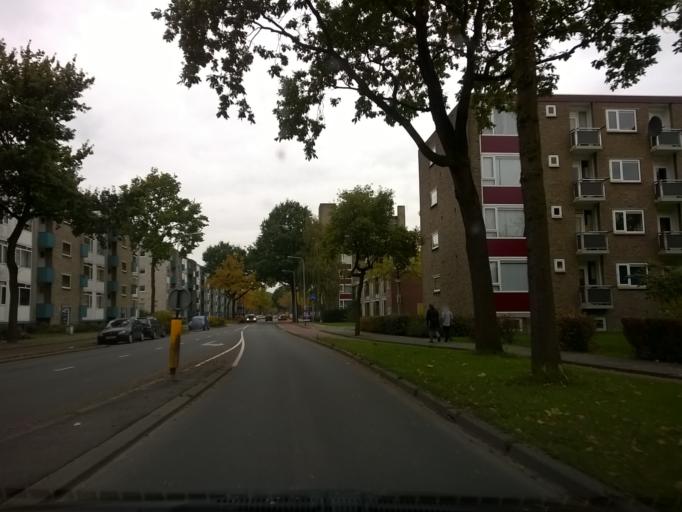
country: NL
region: Groningen
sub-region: Gemeente Groningen
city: Korrewegwijk
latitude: 53.2333
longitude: 6.5558
